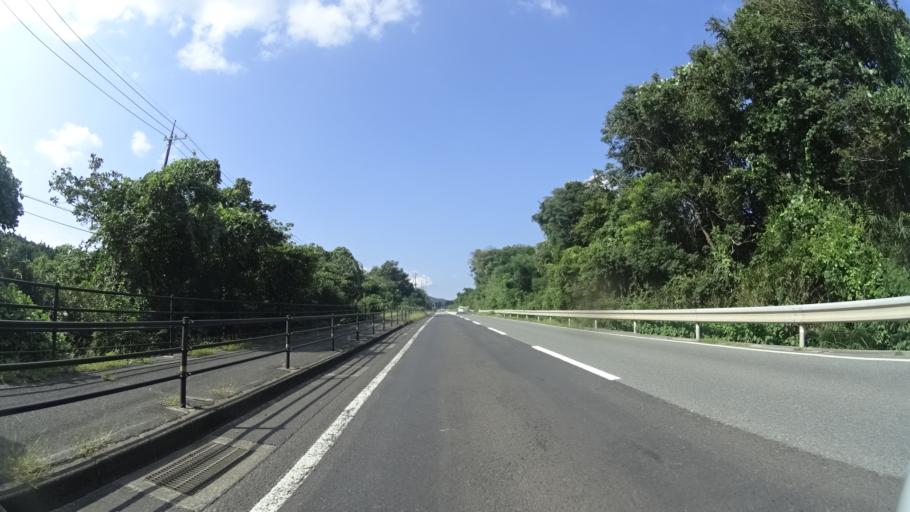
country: JP
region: Shimane
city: Gotsucho
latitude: 35.0429
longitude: 132.2915
